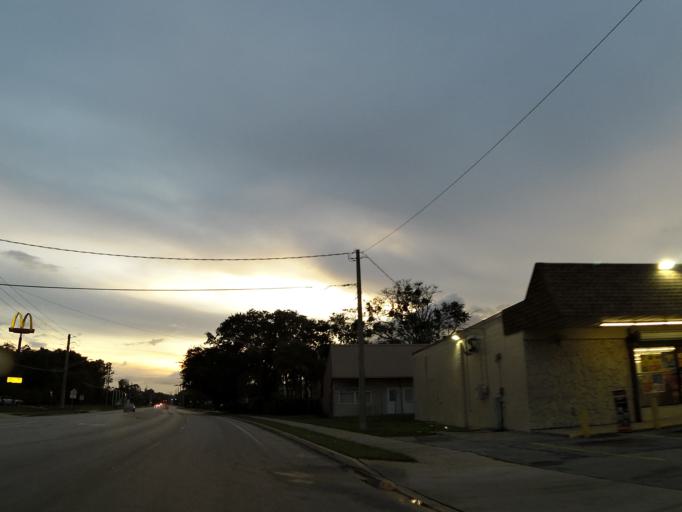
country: US
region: Florida
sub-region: Duval County
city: Jacksonville
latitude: 30.3664
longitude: -81.5968
